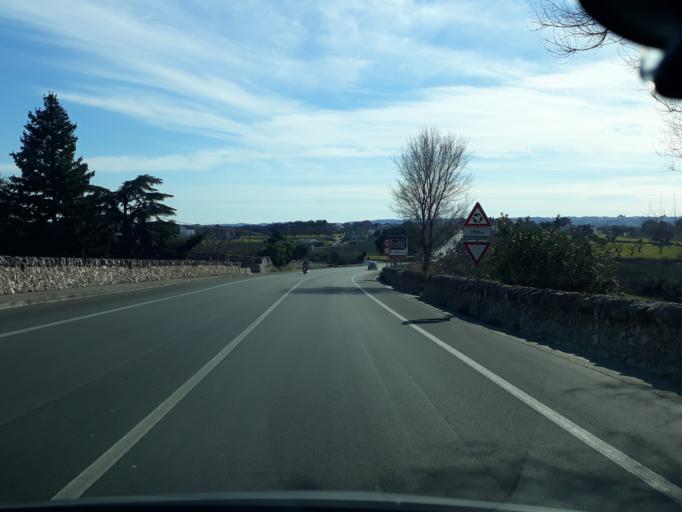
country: IT
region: Apulia
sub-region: Provincia di Bari
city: Locorotondo
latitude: 40.7510
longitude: 17.3285
